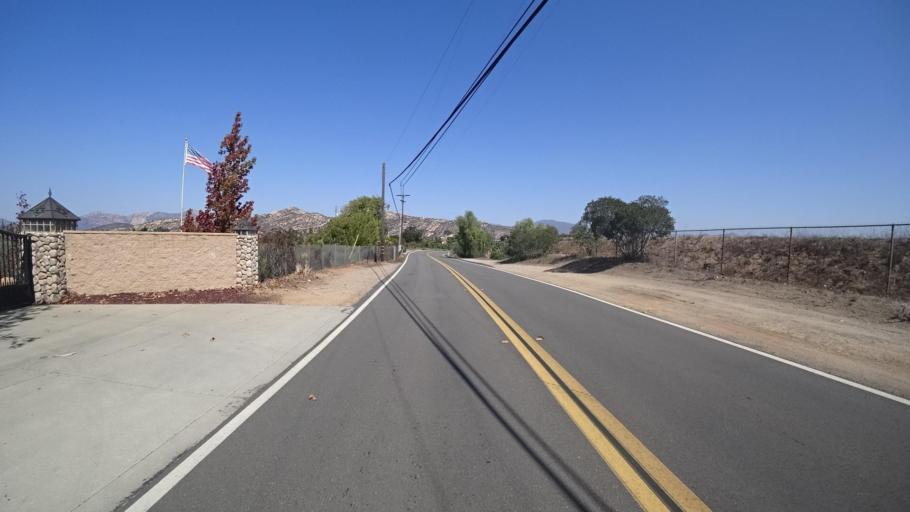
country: US
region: California
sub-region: San Diego County
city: Crest
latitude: 32.8199
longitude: -116.8532
